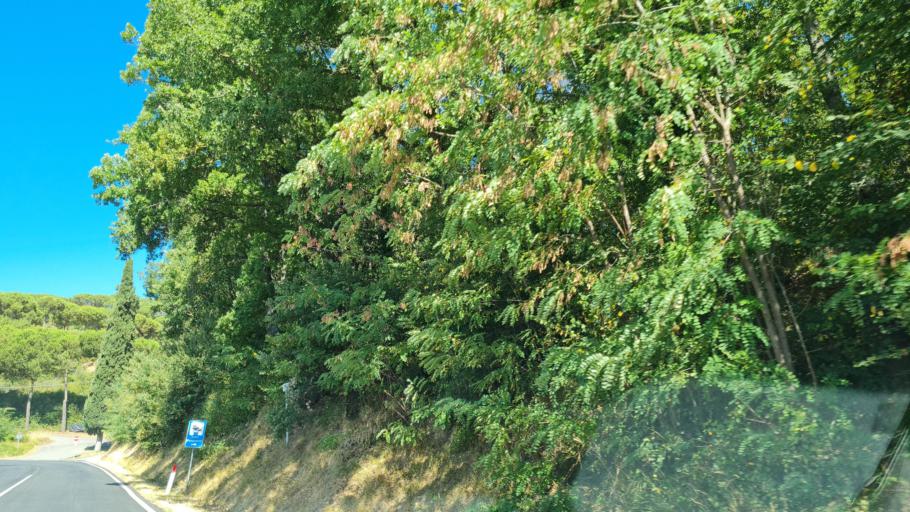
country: IT
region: Tuscany
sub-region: Provincia di Siena
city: Sant'Albino
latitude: 43.0749
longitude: 11.7967
